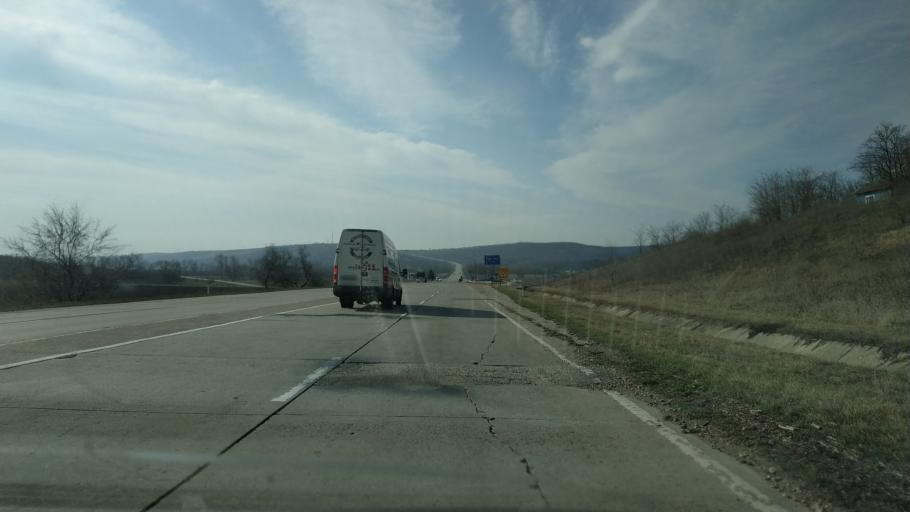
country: MD
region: Chisinau
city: Singera
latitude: 46.8180
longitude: 28.9106
